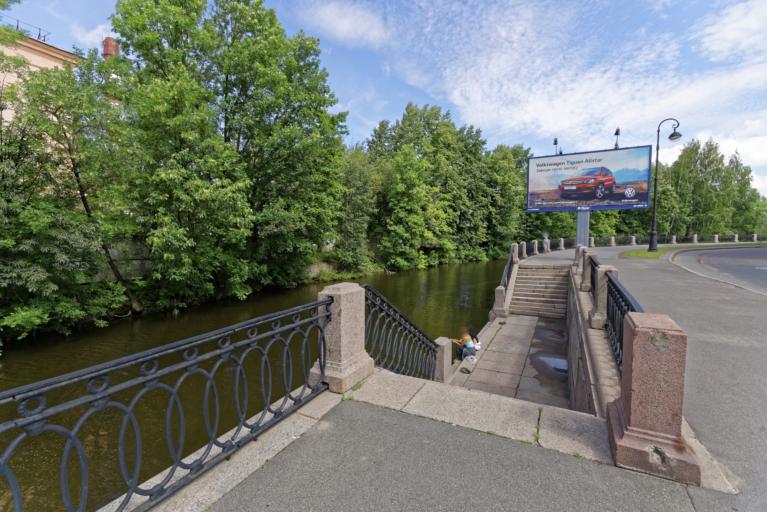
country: RU
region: St.-Petersburg
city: Vasyl'evsky Ostrov
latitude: 59.9496
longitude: 30.2707
